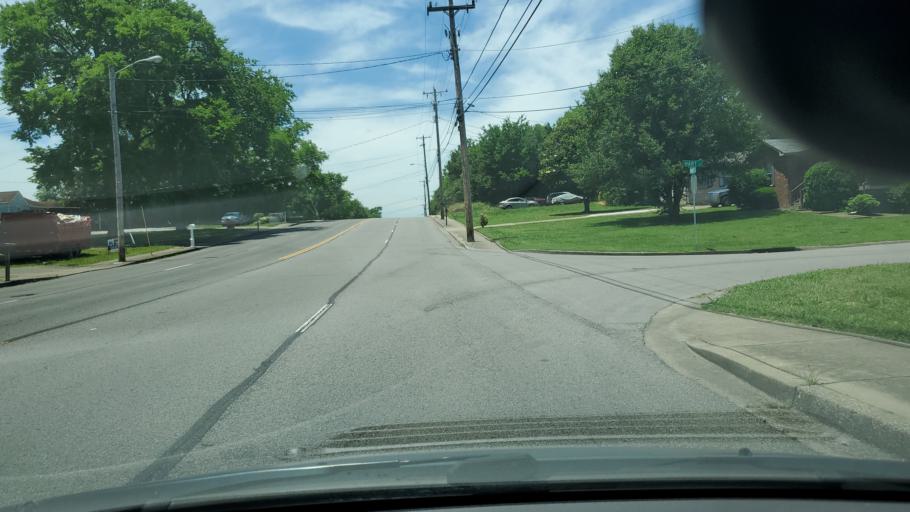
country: US
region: Tennessee
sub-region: Davidson County
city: Nashville
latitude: 36.2209
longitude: -86.7561
